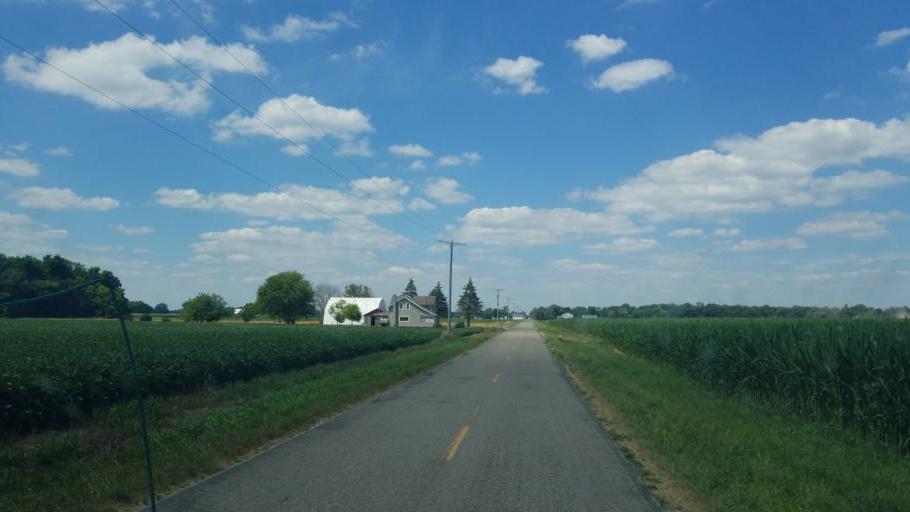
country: US
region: Ohio
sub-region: Defiance County
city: Hicksville
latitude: 41.3006
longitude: -84.7281
